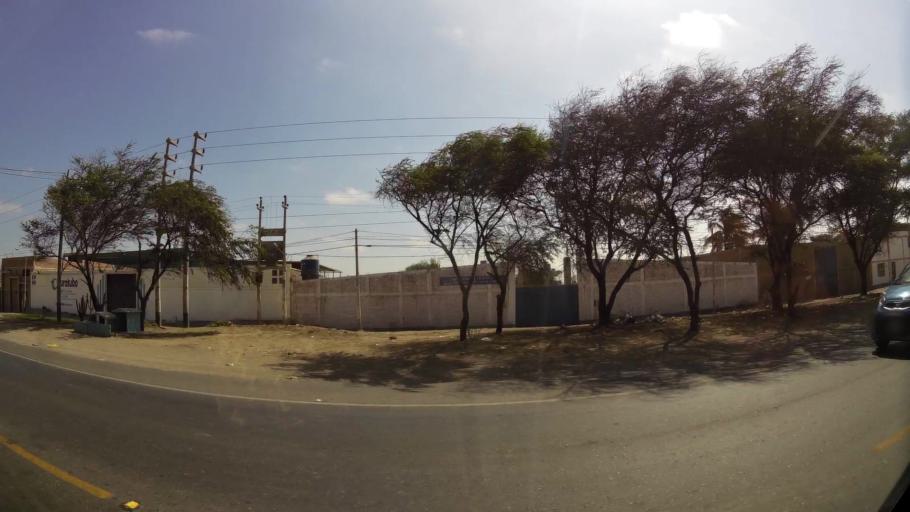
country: PE
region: Lambayeque
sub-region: Provincia de Chiclayo
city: Reque
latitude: -6.8286
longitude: -79.8294
